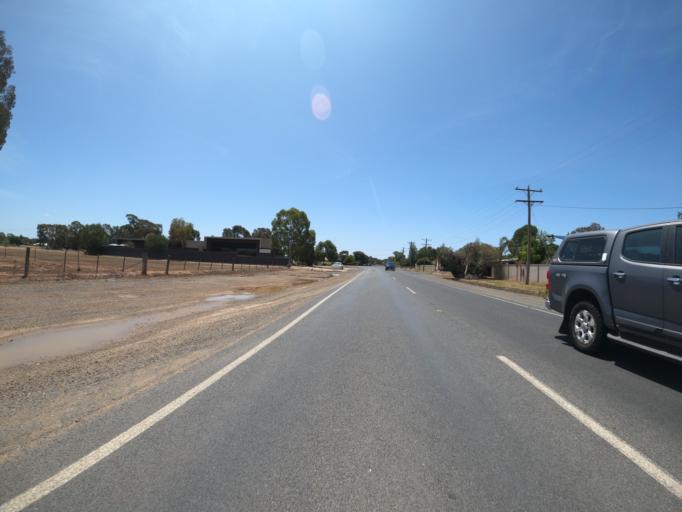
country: AU
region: Victoria
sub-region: Moira
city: Yarrawonga
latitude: -36.0218
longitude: 145.9955
